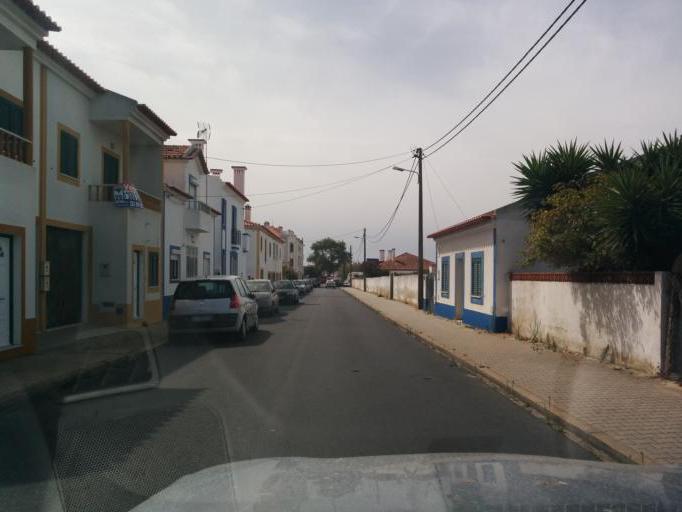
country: PT
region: Beja
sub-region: Odemira
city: Vila Nova de Milfontes
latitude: 37.7273
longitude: -8.7850
